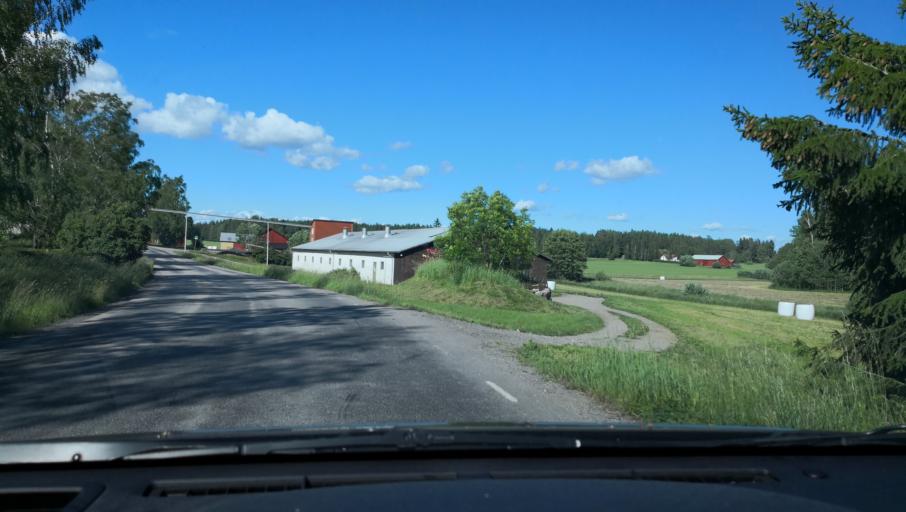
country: SE
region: Soedermanland
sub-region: Eskilstuna Kommun
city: Arla
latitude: 59.3199
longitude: 16.6085
